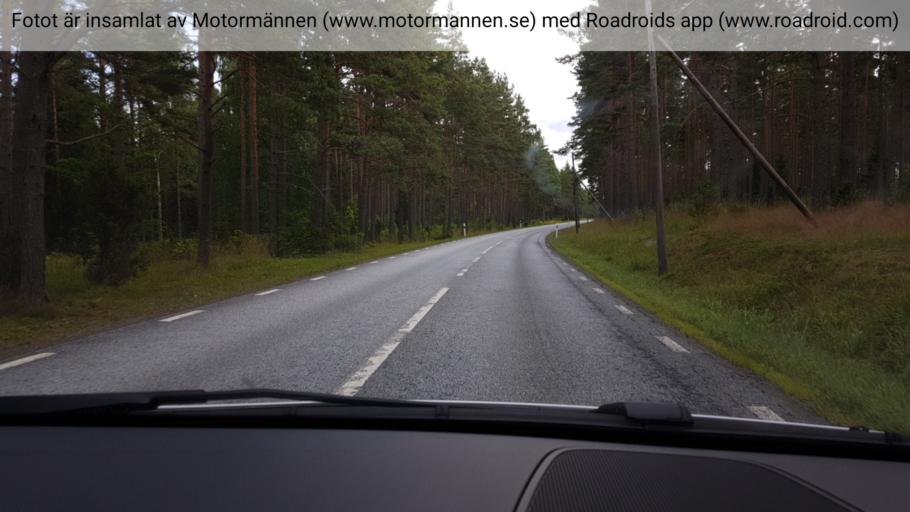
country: SE
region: Uppsala
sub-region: Osthammars Kommun
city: Anneberg
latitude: 60.1681
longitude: 18.4112
